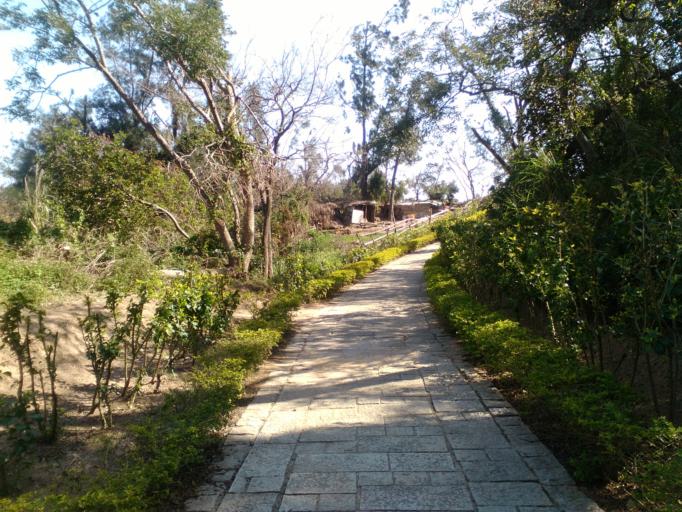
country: CN
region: Fujian
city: Shijing
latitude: 24.5054
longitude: 118.4374
